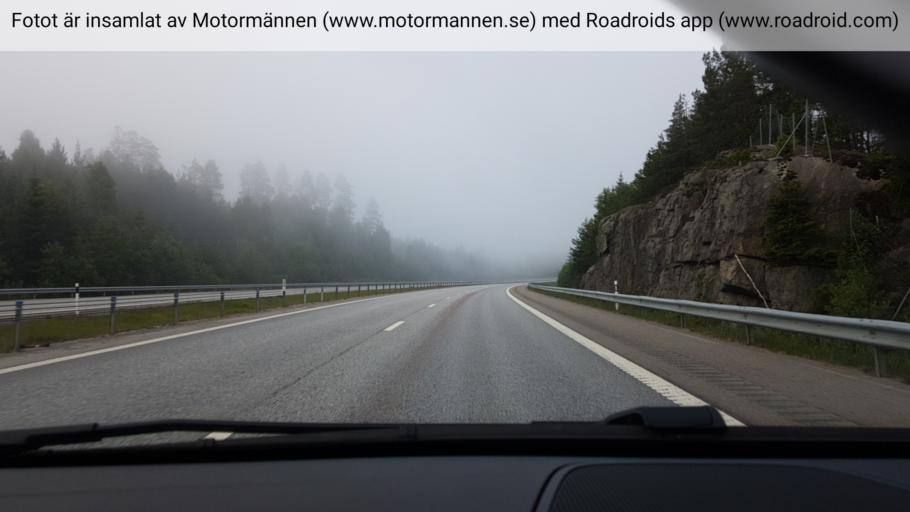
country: SE
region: Soedermanland
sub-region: Trosa Kommun
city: Vagnharad
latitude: 58.9788
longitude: 17.5296
